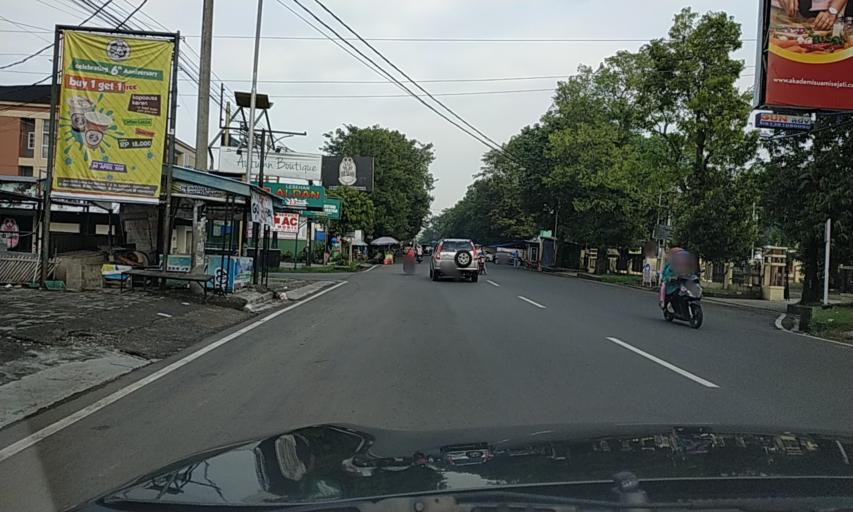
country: ID
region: Central Java
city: Purwokerto
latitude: -7.4175
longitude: 109.2516
